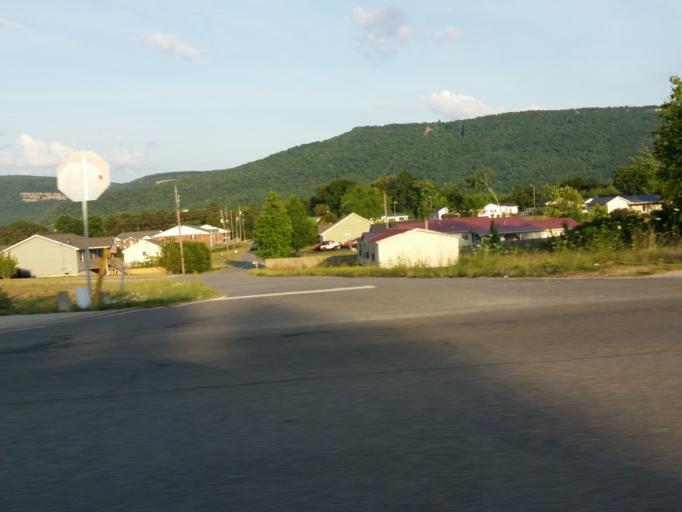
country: US
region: Georgia
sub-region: Dade County
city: Trenton
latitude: 34.8648
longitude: -85.5149
